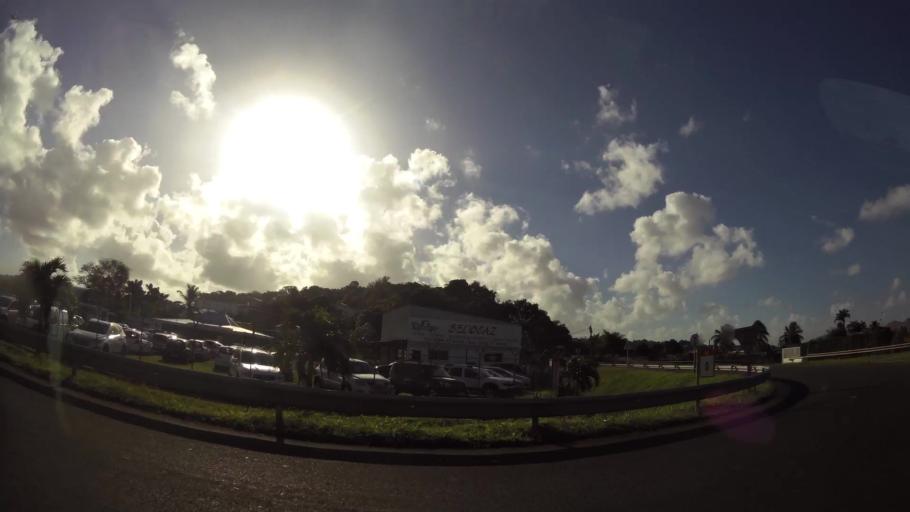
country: MQ
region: Martinique
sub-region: Martinique
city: Ducos
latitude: 14.5942
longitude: -60.9823
